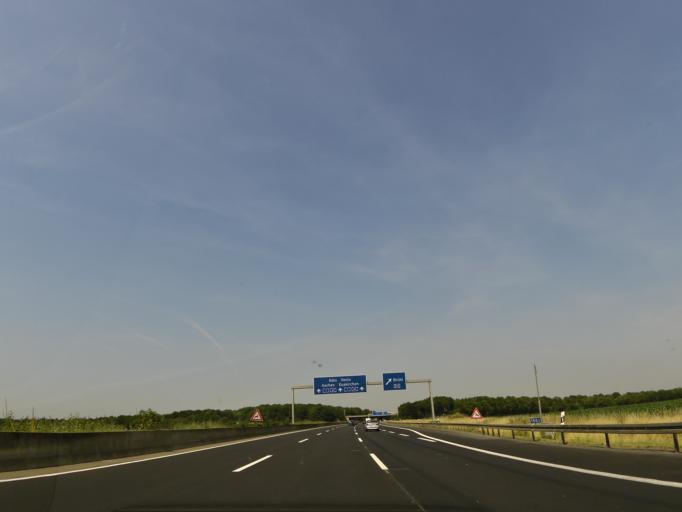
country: DE
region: North Rhine-Westphalia
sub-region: Regierungsbezirk Koln
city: Weilerswist
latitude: 50.7674
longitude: 6.8319
